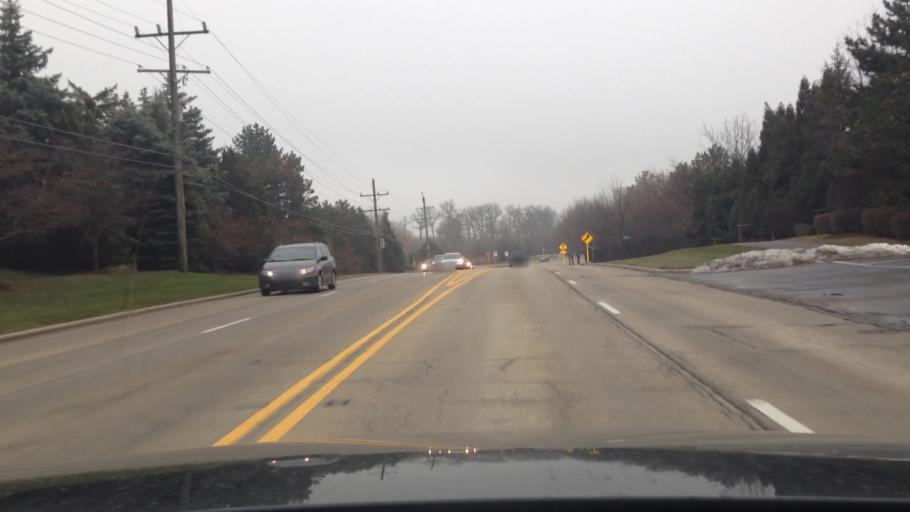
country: US
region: Illinois
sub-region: DuPage County
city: Oakbrook Terrace
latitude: 41.8277
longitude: -87.9717
